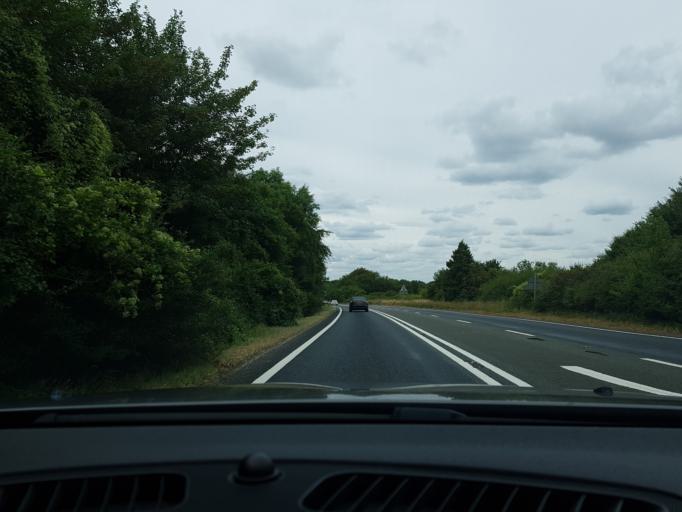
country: GB
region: England
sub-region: Hampshire
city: Kingsclere
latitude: 51.3132
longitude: -1.2019
